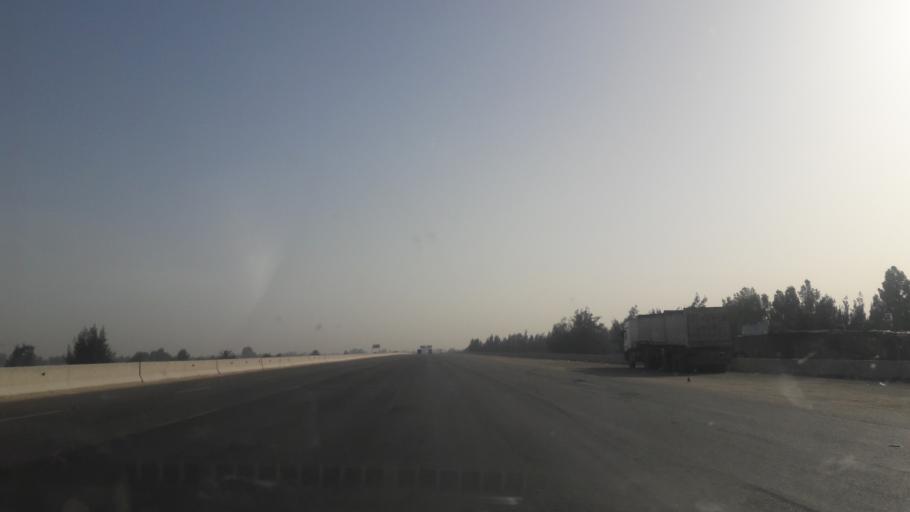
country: EG
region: Al Isma'iliyah
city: Ismailia
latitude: 30.7011
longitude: 32.1111
